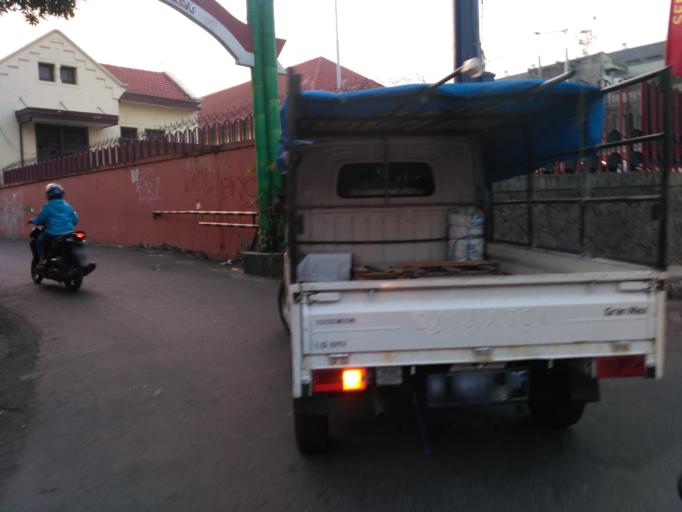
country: ID
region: East Java
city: Malang
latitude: -7.9907
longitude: 112.6343
